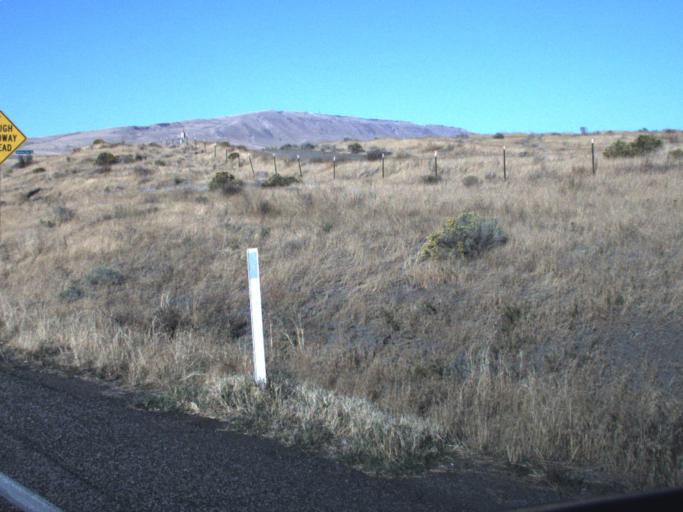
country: US
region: Washington
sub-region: Benton County
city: West Richland
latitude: 46.3830
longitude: -119.4235
